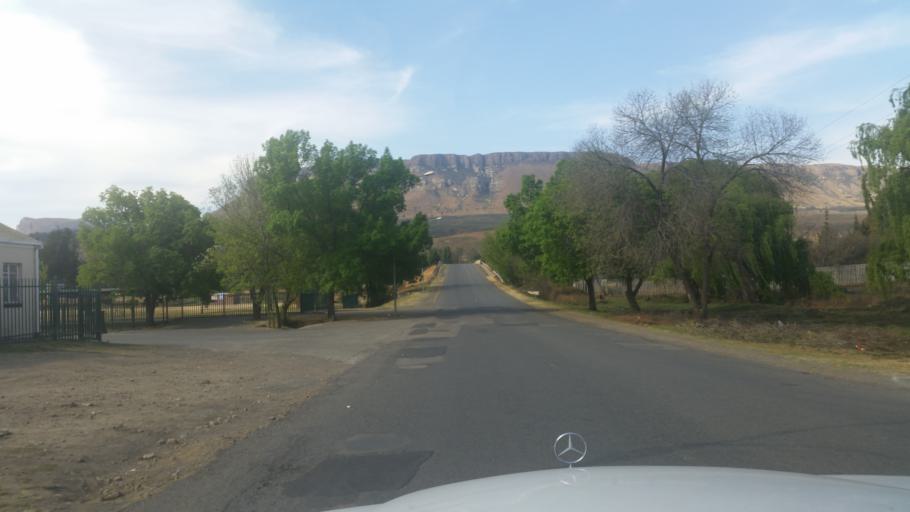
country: ZA
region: Orange Free State
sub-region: Thabo Mofutsanyana District Municipality
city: Harrismith
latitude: -28.2687
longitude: 29.1321
